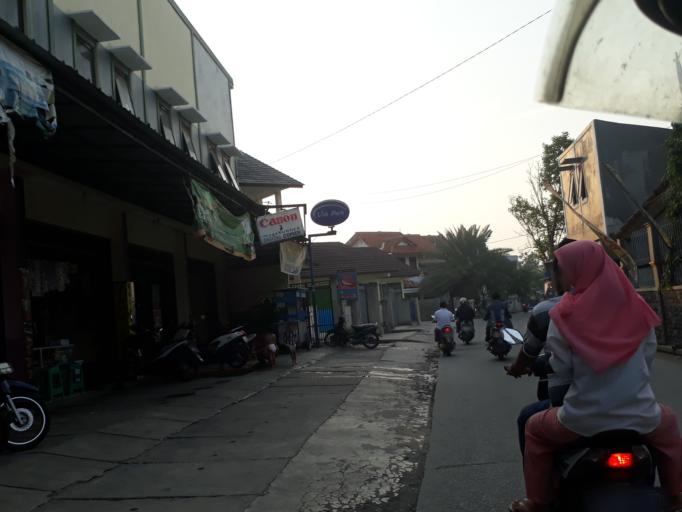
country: ID
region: West Java
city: Bekasi
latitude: -6.2452
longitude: 107.0572
